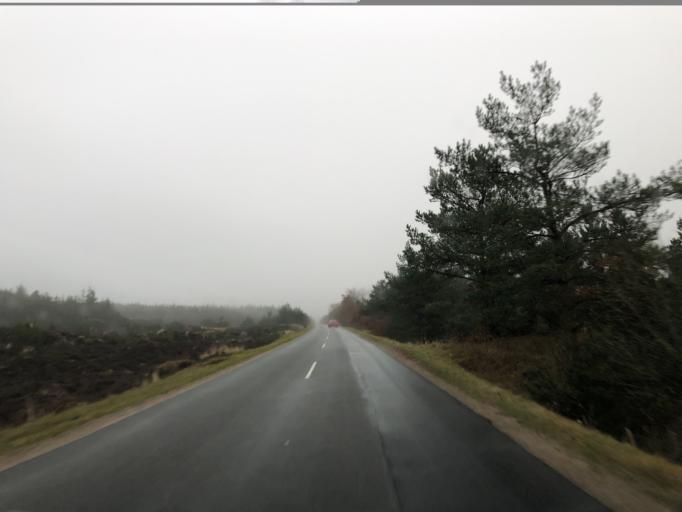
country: DK
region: Central Jutland
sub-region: Holstebro Kommune
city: Ulfborg
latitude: 56.2174
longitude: 8.3894
